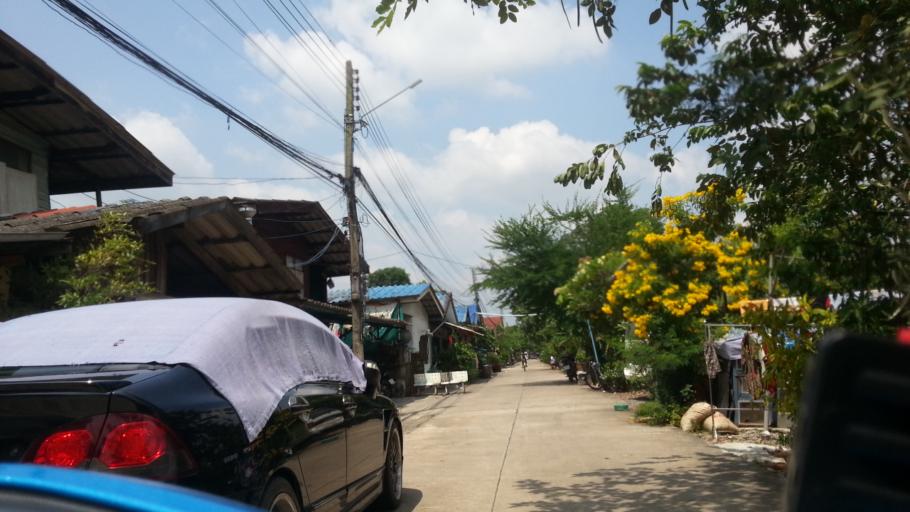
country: TH
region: Pathum Thani
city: Ban Rangsit
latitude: 14.0553
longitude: 100.8267
